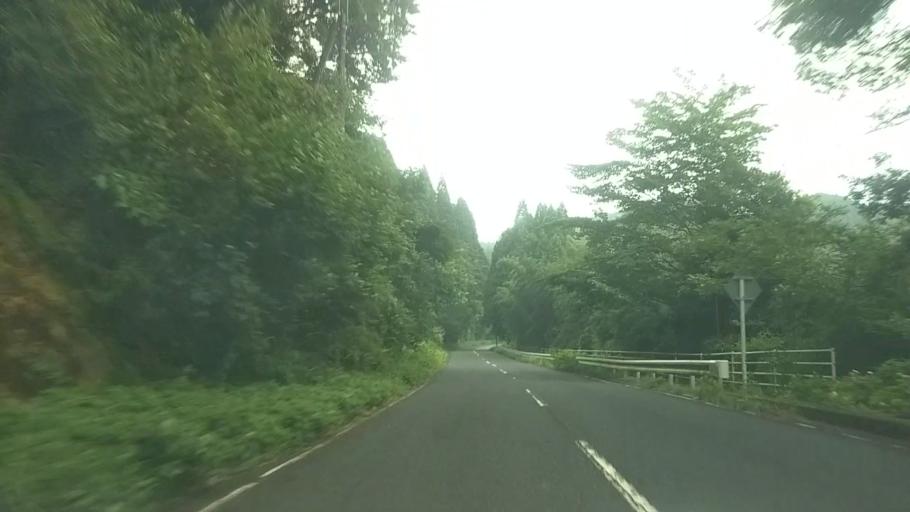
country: JP
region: Chiba
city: Katsuura
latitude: 35.2539
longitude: 140.2447
